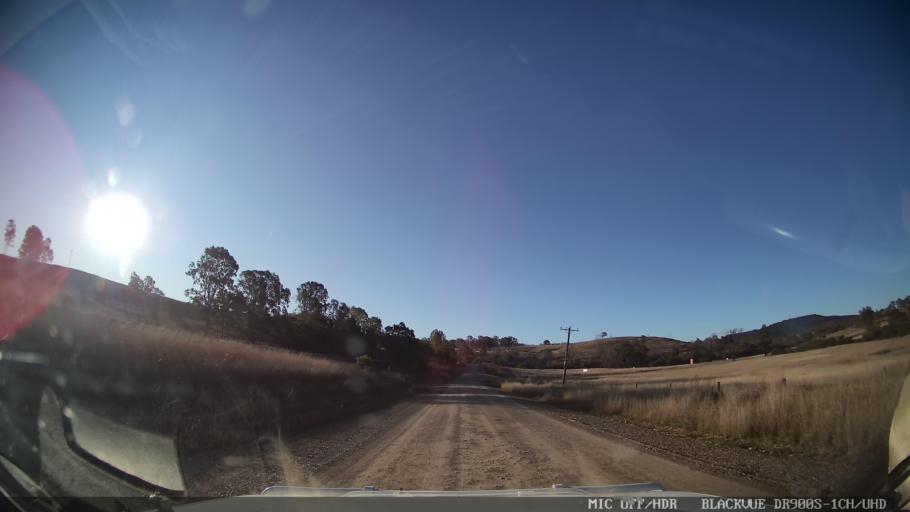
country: AU
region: Queensland
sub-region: Gladstone
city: Toolooa
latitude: -24.6913
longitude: 151.3062
